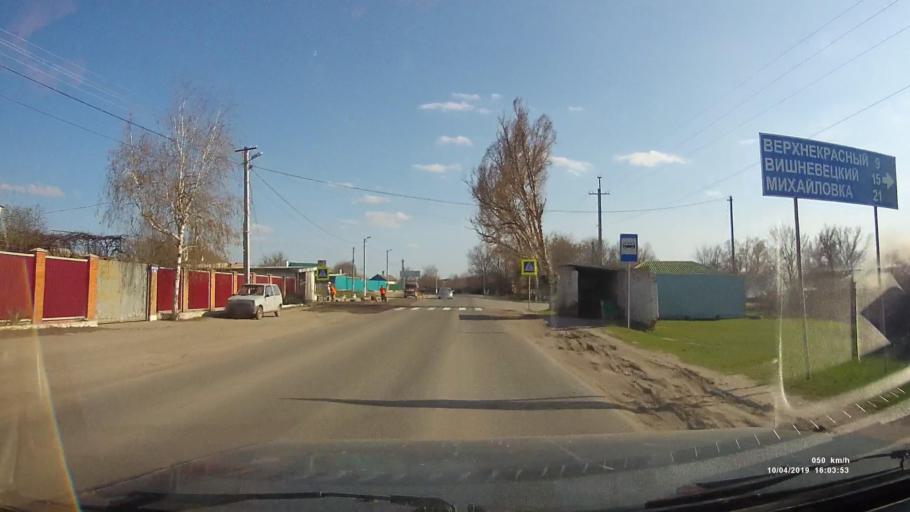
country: RU
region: Rostov
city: Staraya Stanitsa
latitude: 48.3596
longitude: 40.2656
